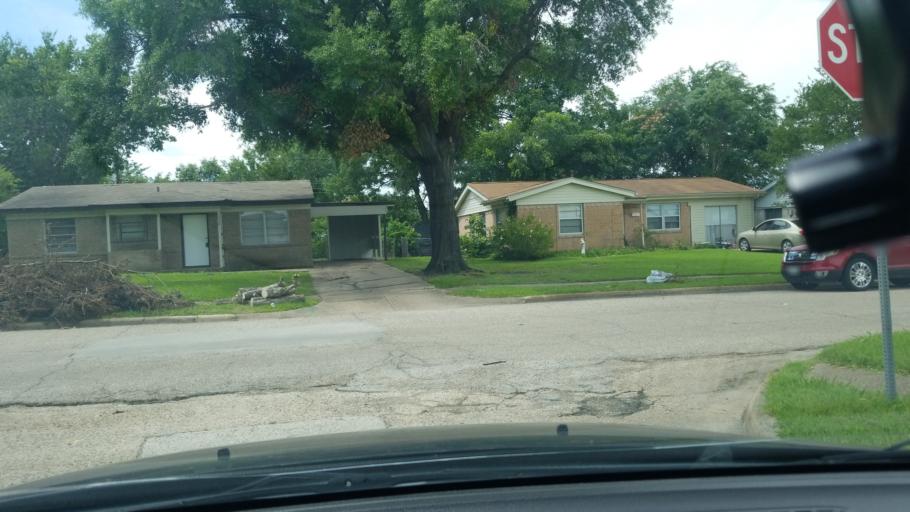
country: US
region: Texas
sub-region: Dallas County
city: Mesquite
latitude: 32.7536
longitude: -96.5818
